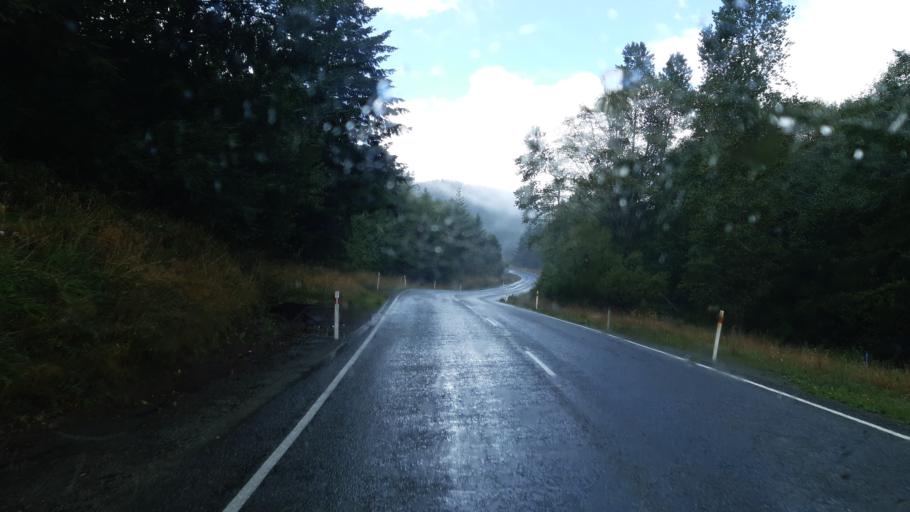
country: NZ
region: Tasman
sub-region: Tasman District
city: Wakefield
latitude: -41.4866
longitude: 172.8897
